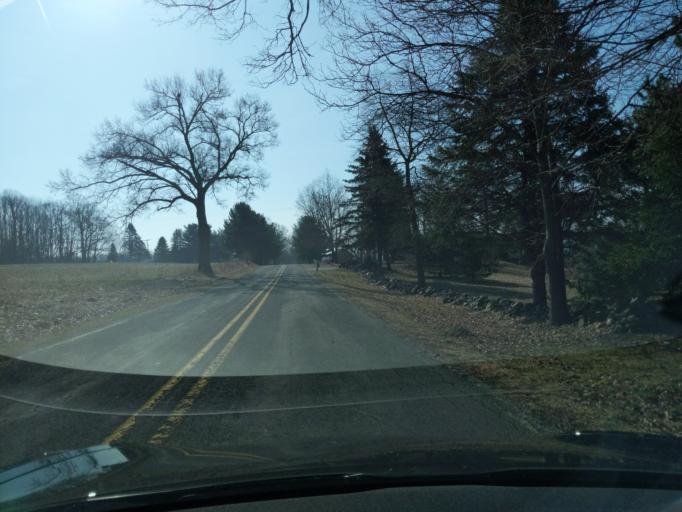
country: US
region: Michigan
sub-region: Ingham County
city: Leslie
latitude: 42.3740
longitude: -84.4407
